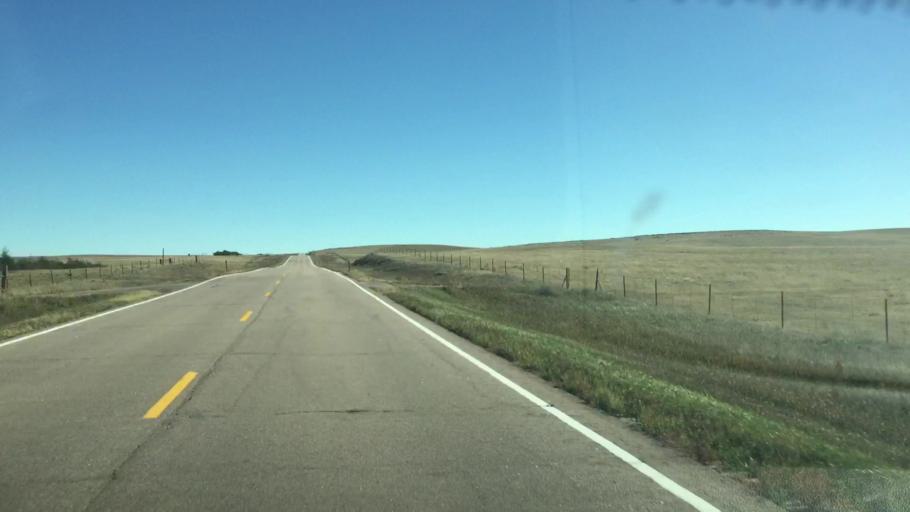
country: US
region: Colorado
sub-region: Lincoln County
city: Limon
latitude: 39.2813
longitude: -103.9905
